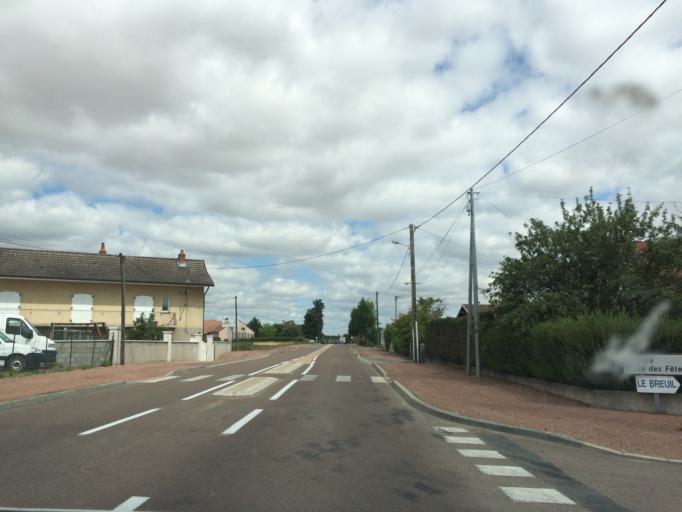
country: FR
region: Bourgogne
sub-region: Departement de la Cote-d'Or
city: Fenay
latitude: 47.2410
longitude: 5.0579
